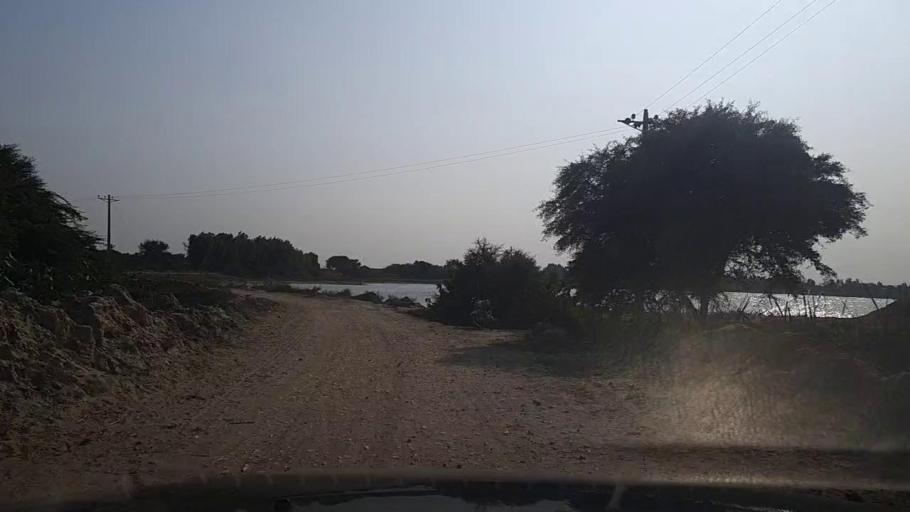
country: PK
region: Sindh
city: Mirpur Sakro
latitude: 24.6295
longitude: 67.7561
